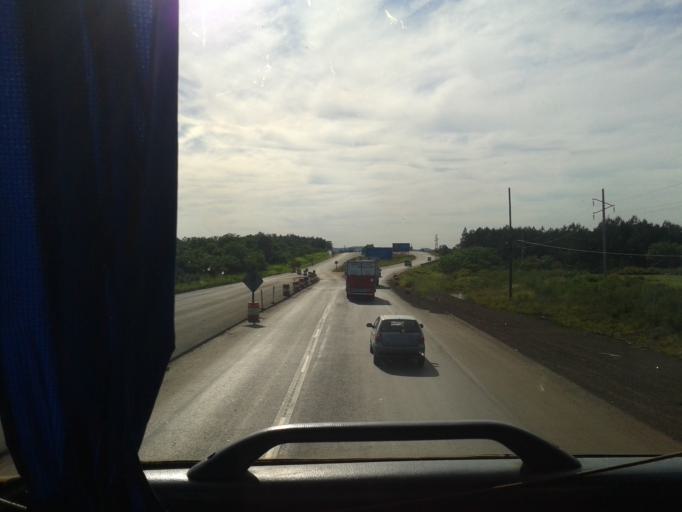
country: AR
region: Misiones
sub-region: Departamento de Candelaria
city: Candelaria
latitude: -27.4624
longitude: -55.6883
